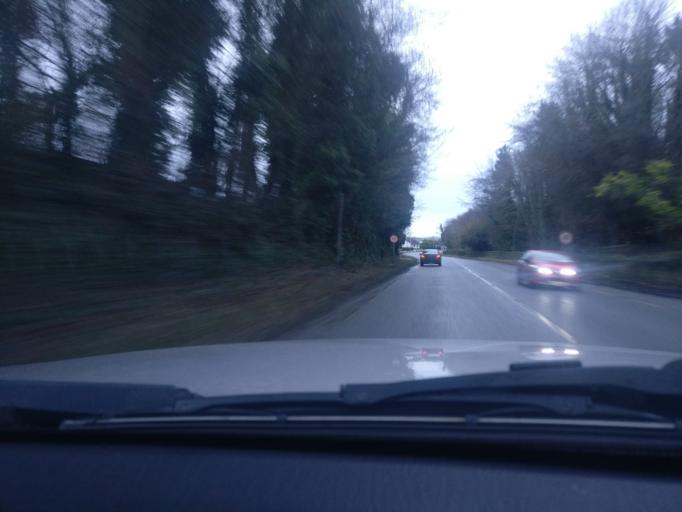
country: IE
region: Leinster
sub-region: An Mhi
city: Navan
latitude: 53.6569
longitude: -6.7084
